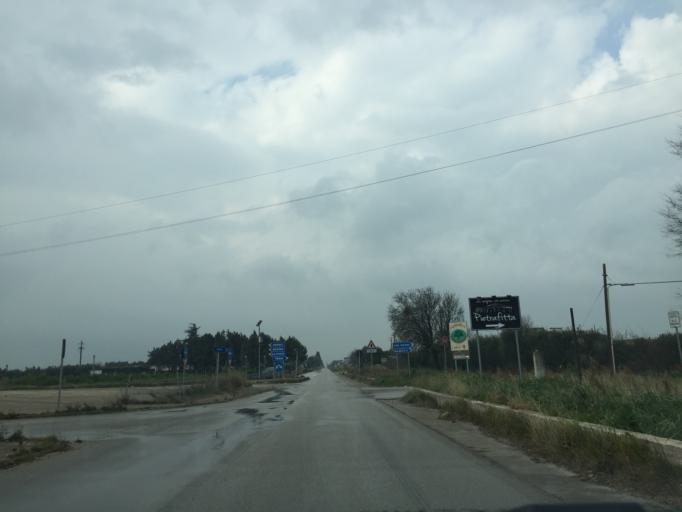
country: IT
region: Apulia
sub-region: Provincia di Foggia
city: Foggia
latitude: 41.4403
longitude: 15.4936
